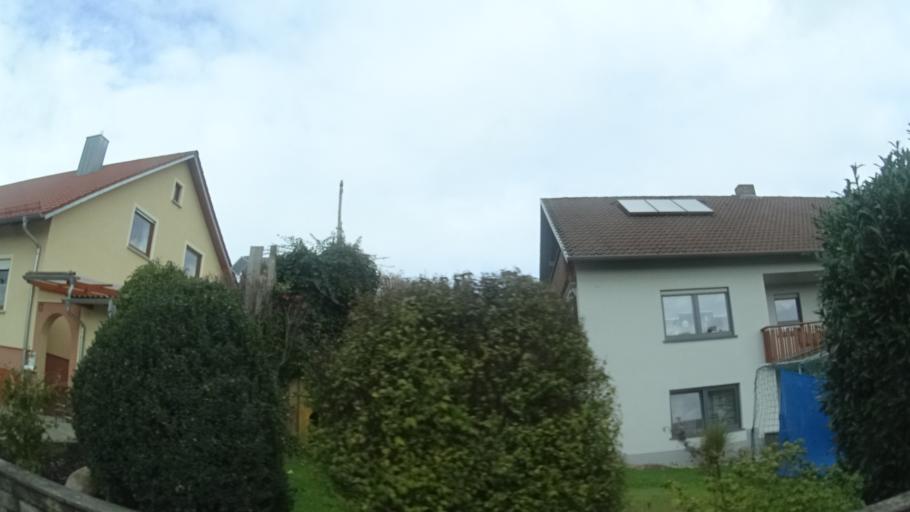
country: DE
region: Bavaria
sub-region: Regierungsbezirk Unterfranken
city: Wuelfershausen
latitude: 50.3335
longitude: 10.3458
